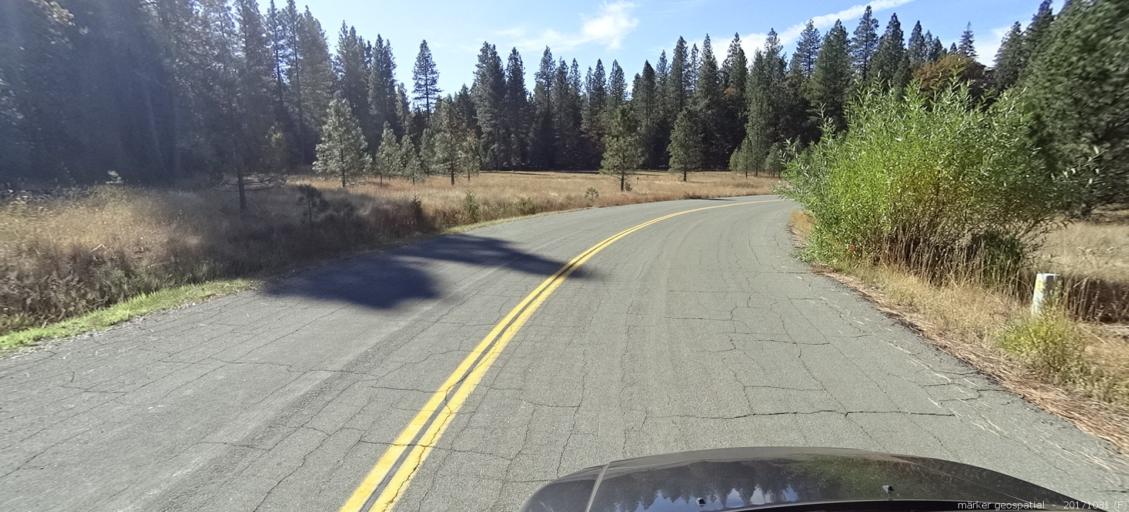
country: US
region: California
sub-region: Shasta County
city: Shingletown
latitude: 40.4910
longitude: -121.8837
